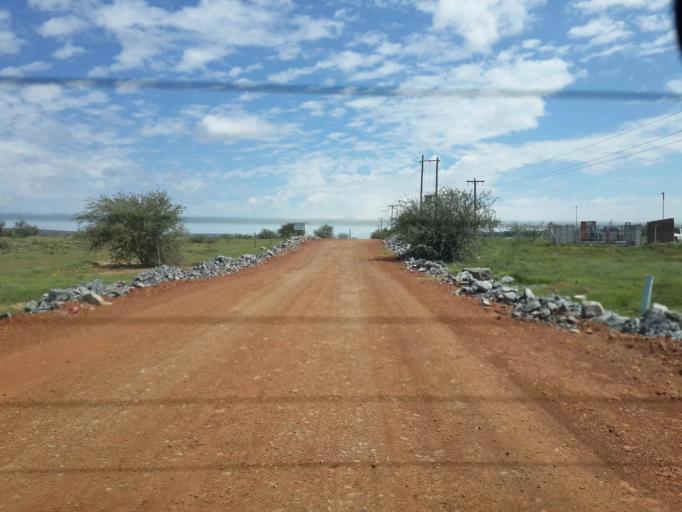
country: ZA
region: Northern Cape
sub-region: Siyanda District Municipality
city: Danielskuil
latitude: -28.2014
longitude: 23.5420
